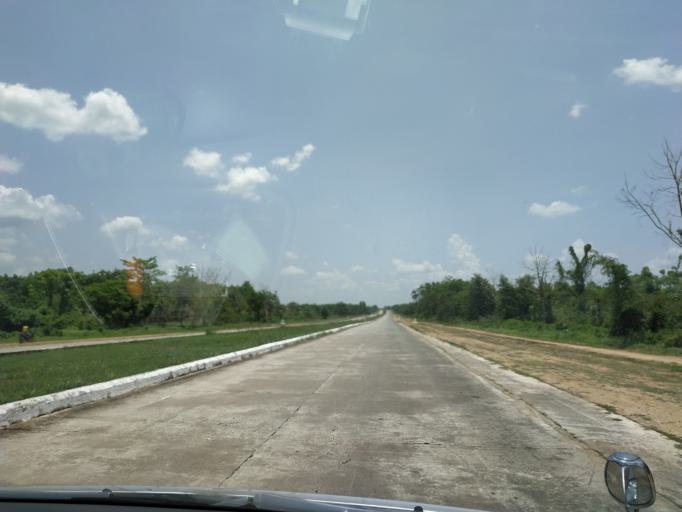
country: MM
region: Bago
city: Thanatpin
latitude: 17.3592
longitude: 96.2632
